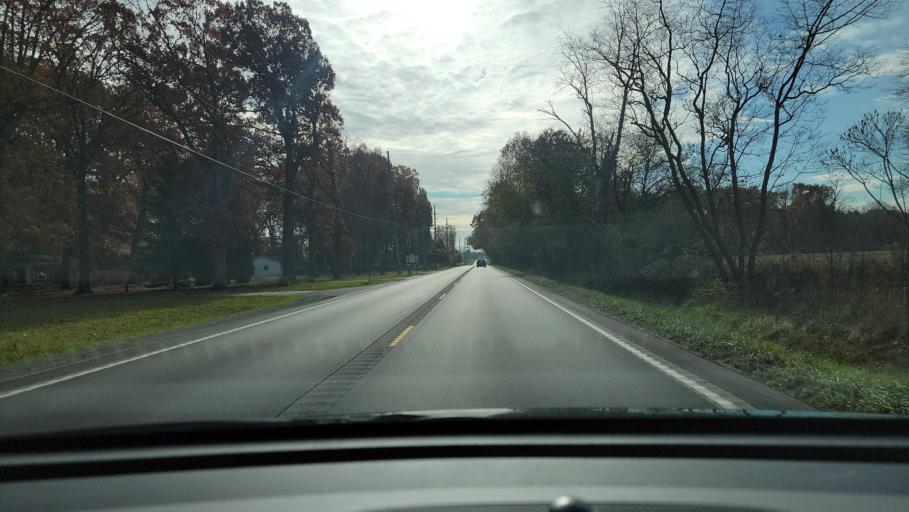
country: US
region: Indiana
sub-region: Porter County
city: South Haven
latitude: 41.5812
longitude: -87.1245
